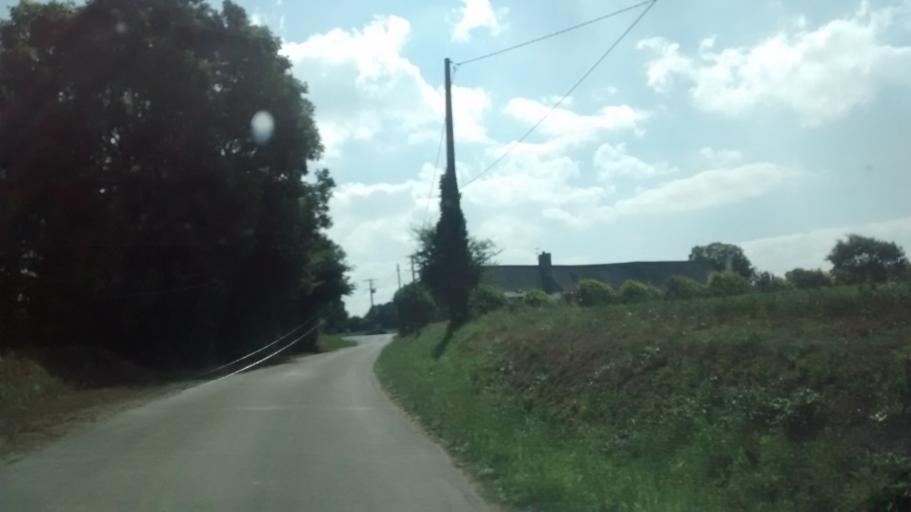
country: FR
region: Brittany
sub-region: Departement d'Ille-et-Vilaine
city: Saint-Coulomb
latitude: 48.6803
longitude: -1.8855
